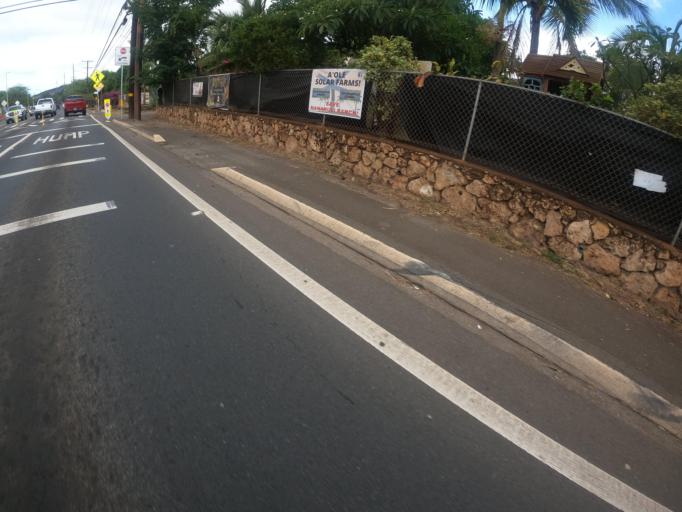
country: US
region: Hawaii
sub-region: Honolulu County
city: Nanakuli
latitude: 21.3751
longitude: -158.1392
